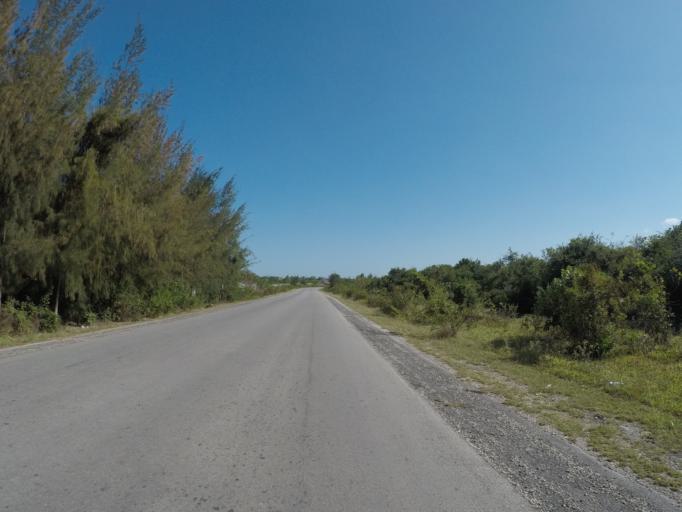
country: TZ
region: Zanzibar Central/South
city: Nganane
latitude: -6.1984
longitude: 39.5319
